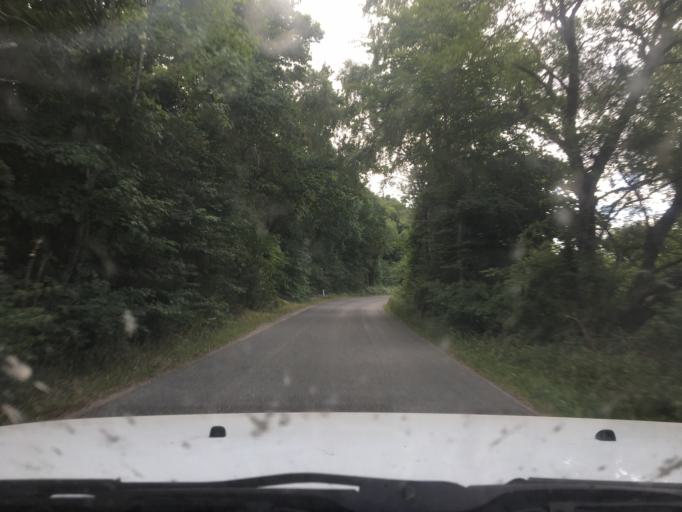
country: DK
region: Central Jutland
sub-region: Syddjurs Kommune
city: Ryomgard
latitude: 56.4493
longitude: 10.6351
